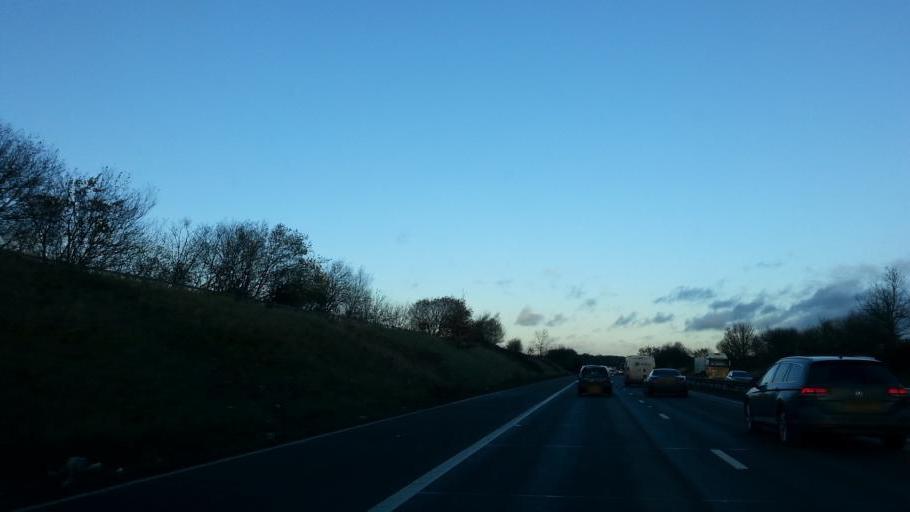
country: GB
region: England
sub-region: Warwickshire
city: Kingsbury
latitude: 52.5550
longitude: -1.7108
